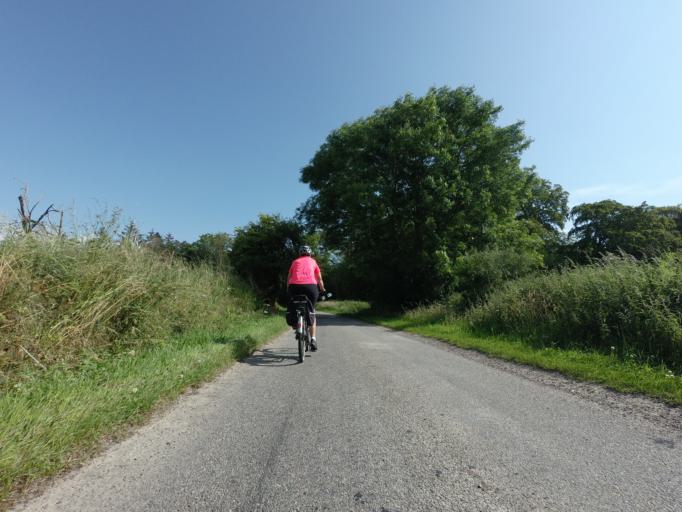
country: GB
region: Scotland
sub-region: Highland
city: Alness
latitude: 57.7151
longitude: -4.2175
